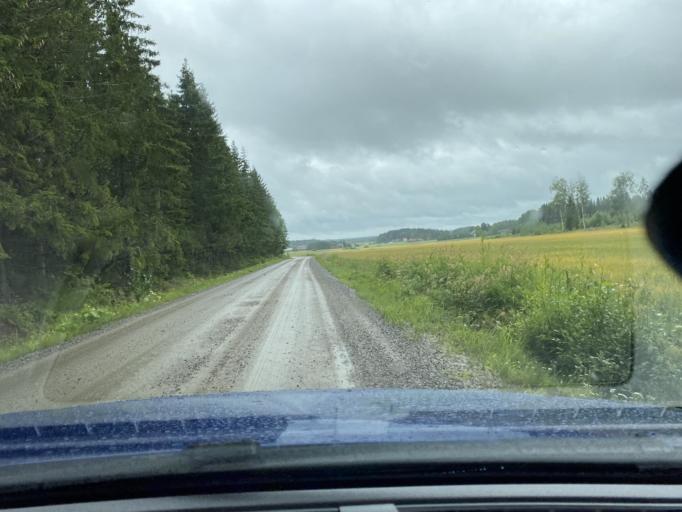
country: FI
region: Pirkanmaa
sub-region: Lounais-Pirkanmaa
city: Punkalaidun
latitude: 61.1489
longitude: 23.2047
